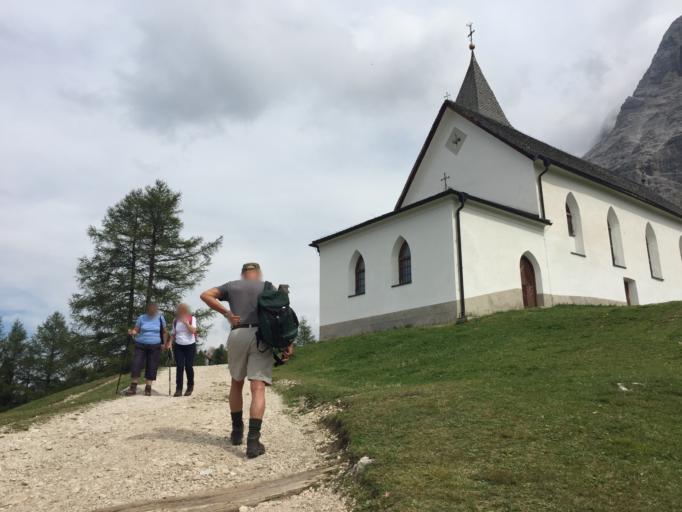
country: IT
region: Trentino-Alto Adige
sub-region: Bolzano
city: Badia
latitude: 46.6141
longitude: 11.9379
